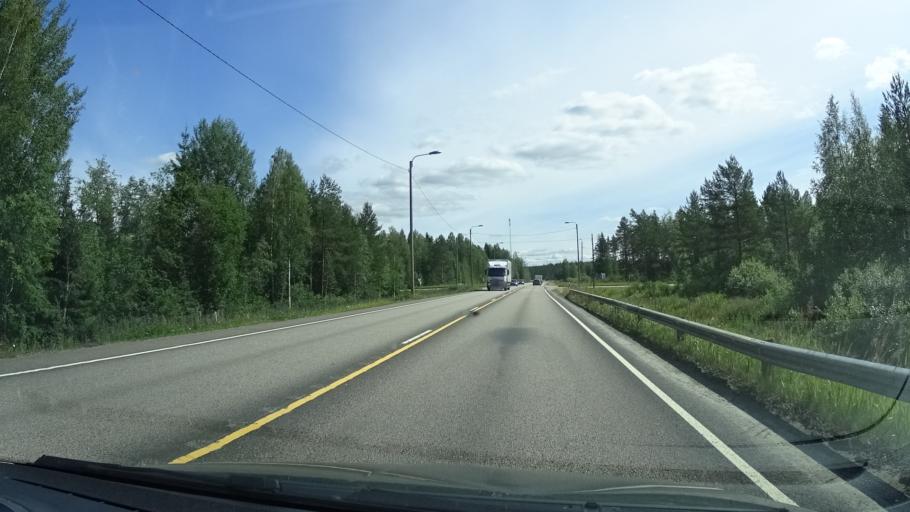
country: FI
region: Central Finland
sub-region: Jyvaeskylae
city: Uurainen
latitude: 62.2654
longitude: 25.4588
